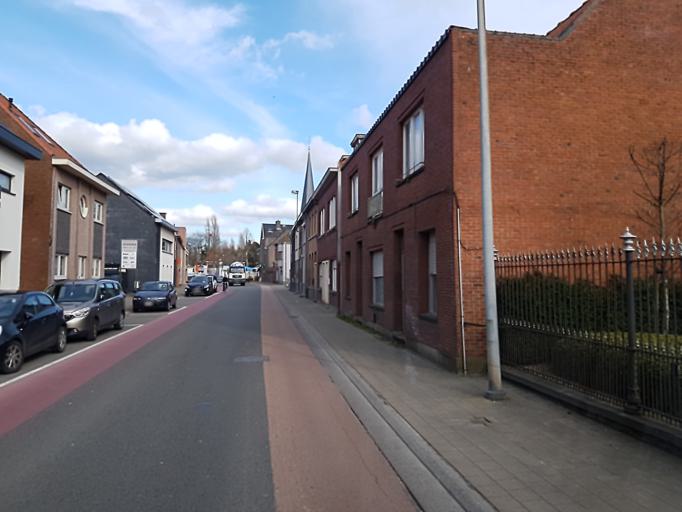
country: BE
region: Flanders
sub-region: Provincie Oost-Vlaanderen
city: Sint-Niklaas
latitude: 51.1933
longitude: 4.1758
